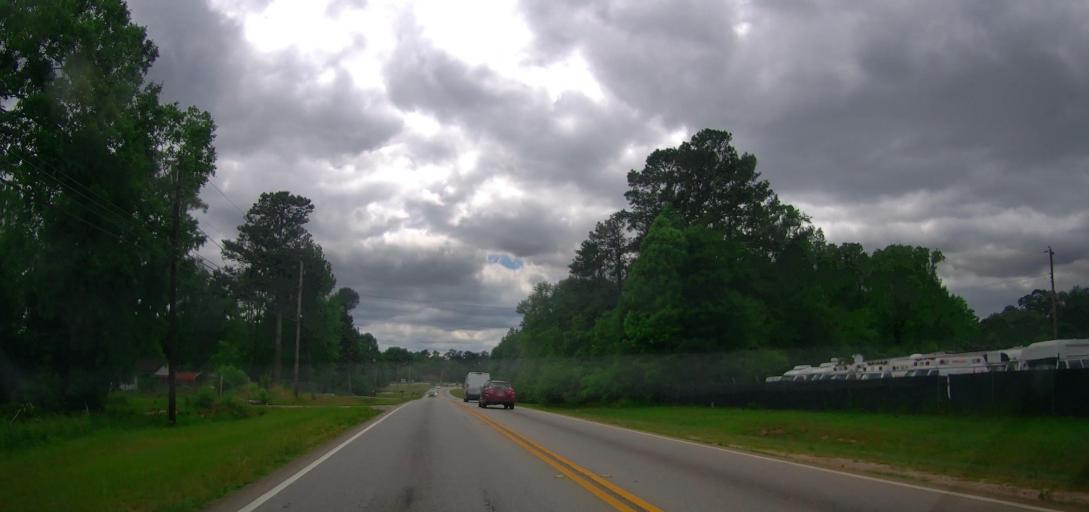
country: US
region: Georgia
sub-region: Henry County
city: Stockbridge
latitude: 33.5435
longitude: -84.1899
